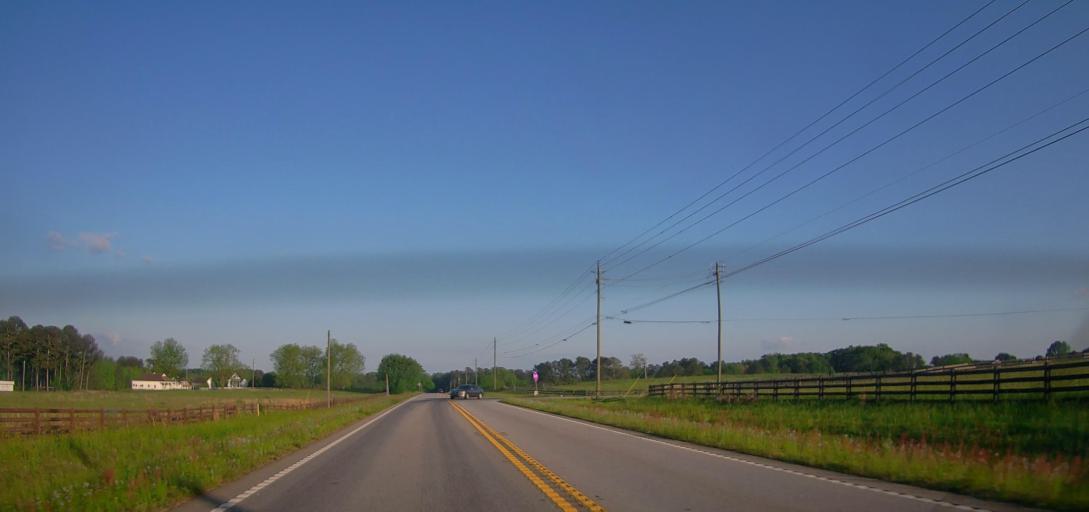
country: US
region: Georgia
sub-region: Walton County
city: Social Circle
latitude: 33.5618
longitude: -83.7519
